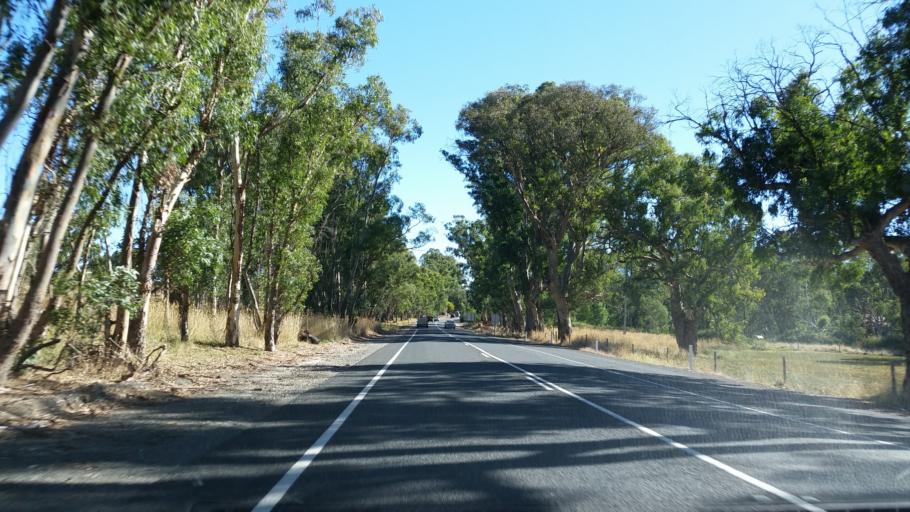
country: AU
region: South Australia
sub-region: Adelaide Hills
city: Birdwood
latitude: -34.8124
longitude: 138.9762
